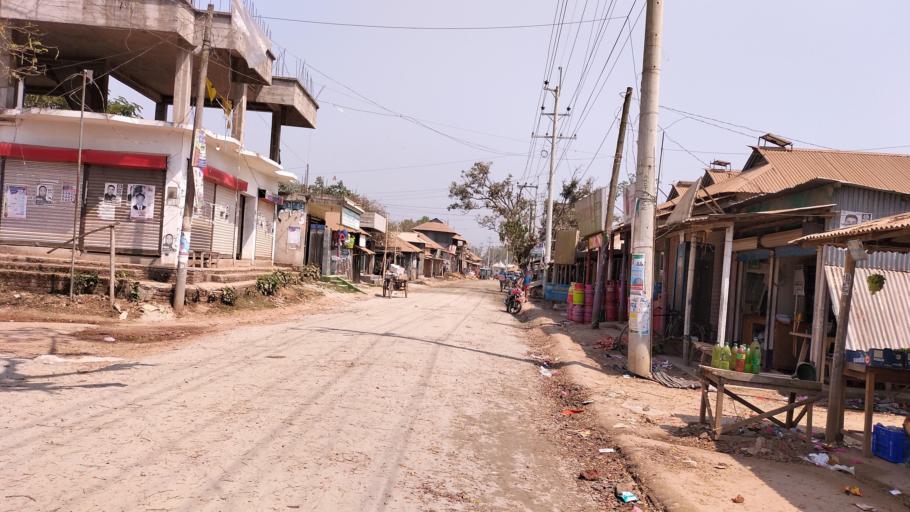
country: BD
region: Dhaka
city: Sakhipur
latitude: 24.3077
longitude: 90.3174
